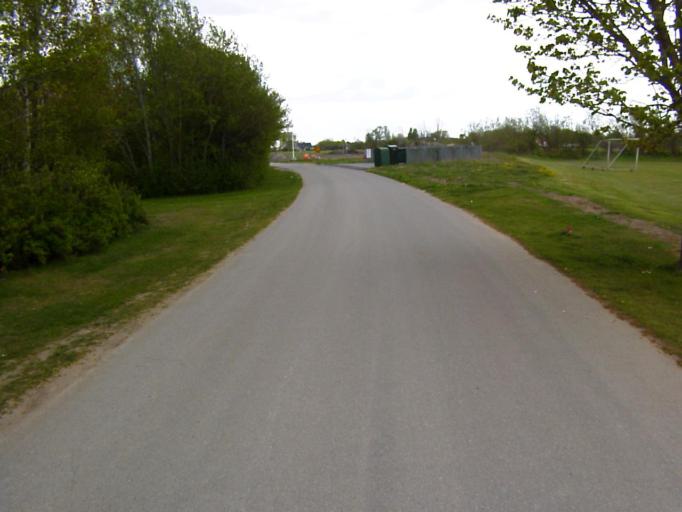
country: SE
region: Skane
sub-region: Kristianstads Kommun
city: Fjalkinge
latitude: 56.0168
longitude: 14.2215
